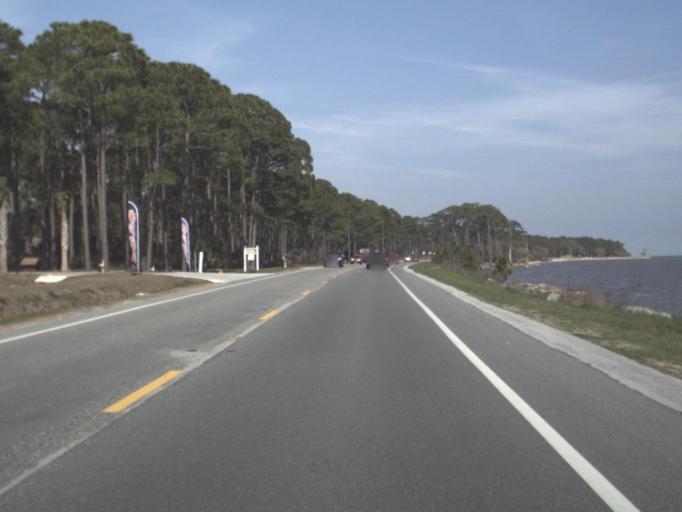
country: US
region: Florida
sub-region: Franklin County
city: Eastpoint
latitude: 29.7557
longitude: -84.8382
